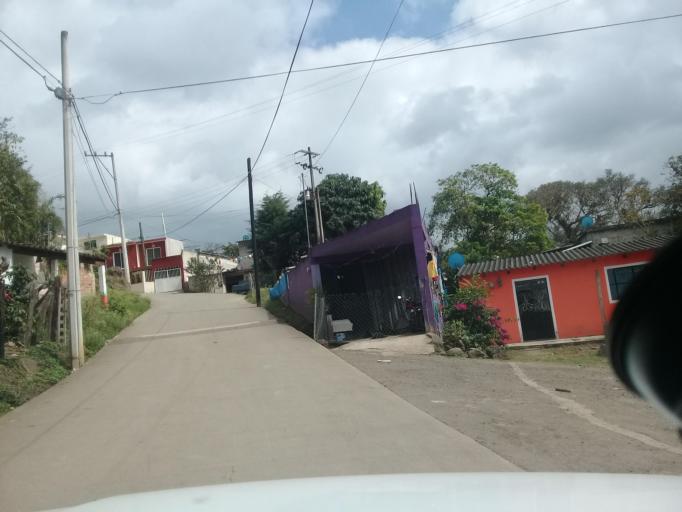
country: MX
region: Veracruz
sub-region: Xalapa
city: Fraccionamiento las Fuentes
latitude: 19.4753
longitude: -96.8776
